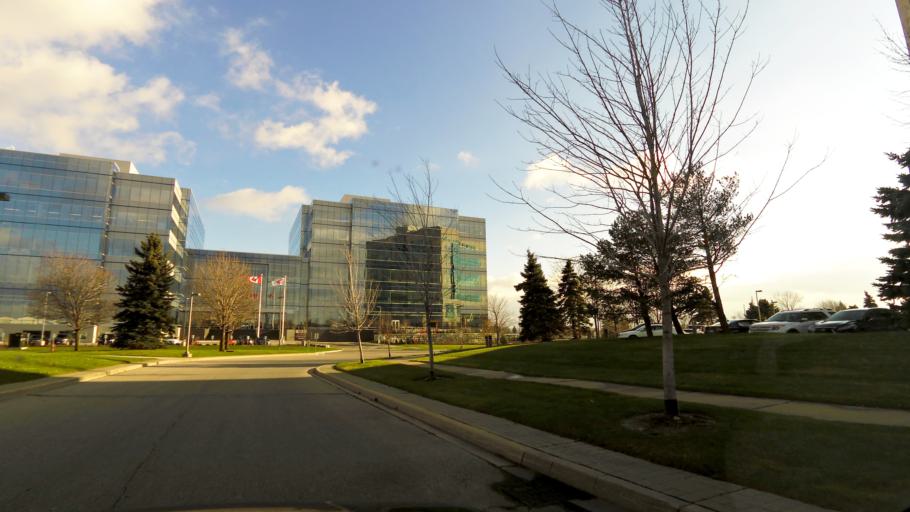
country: CA
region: Ontario
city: Mississauga
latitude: 43.6262
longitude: -79.6838
